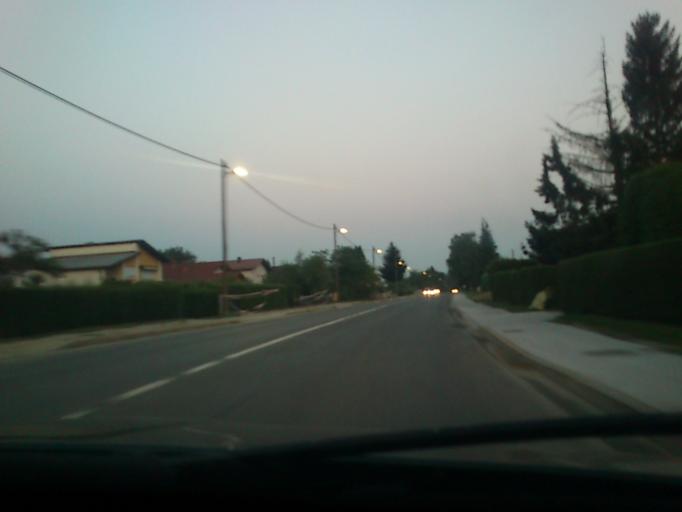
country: SI
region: Duplek
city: Spodnji Duplek
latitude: 46.4825
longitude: 15.7395
